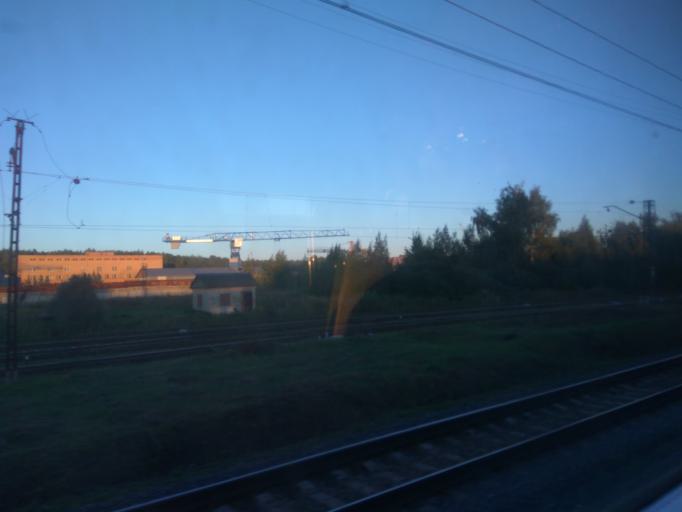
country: RU
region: Moskovskaya
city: Elektrostal'
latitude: 55.7667
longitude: 38.4695
